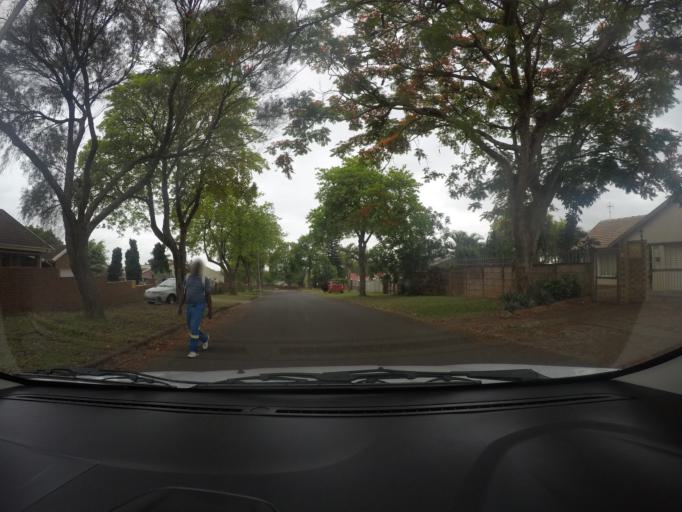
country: ZA
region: KwaZulu-Natal
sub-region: uThungulu District Municipality
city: Empangeni
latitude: -28.7642
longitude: 31.8922
